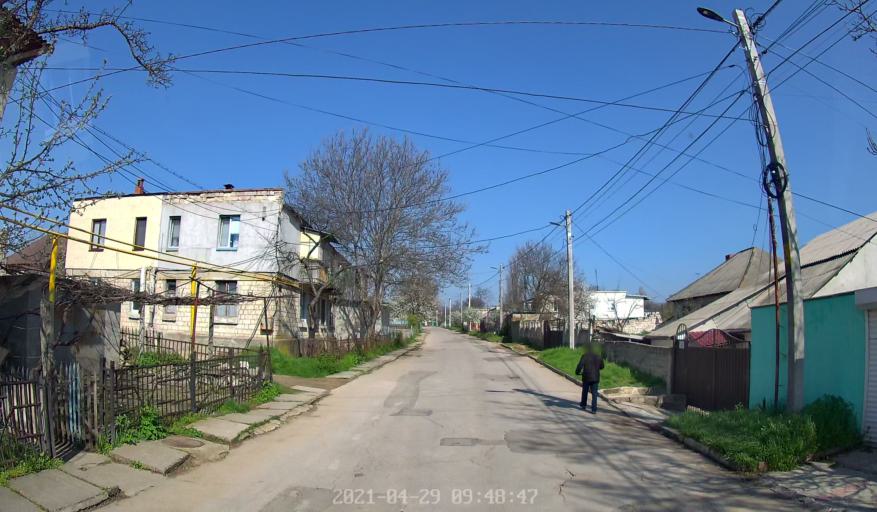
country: MD
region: Chisinau
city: Cricova
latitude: 47.1412
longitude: 28.8607
